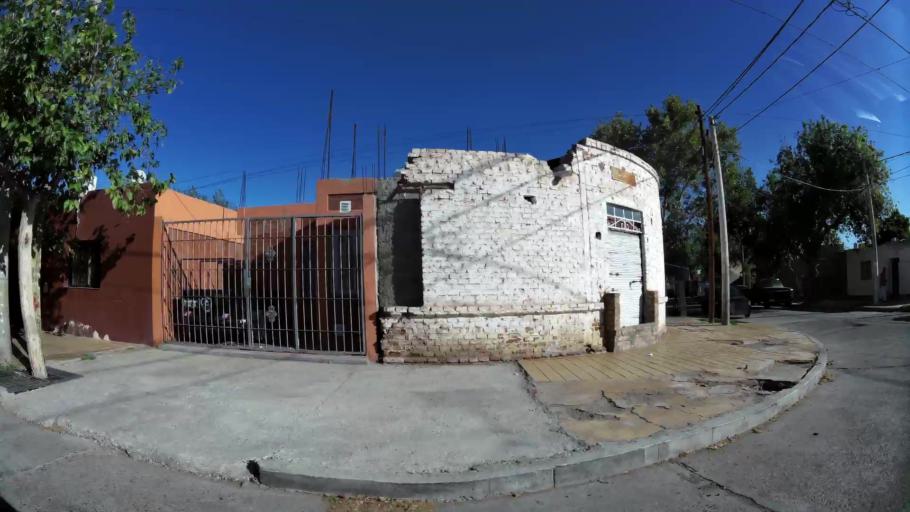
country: AR
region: San Juan
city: San Juan
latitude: -31.5458
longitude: -68.5163
